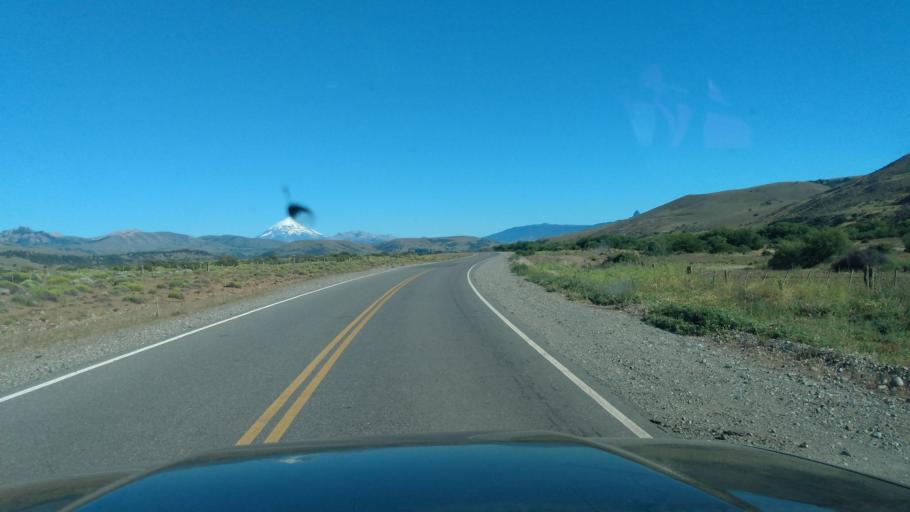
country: AR
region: Neuquen
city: Junin de los Andes
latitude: -39.8931
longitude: -71.1499
